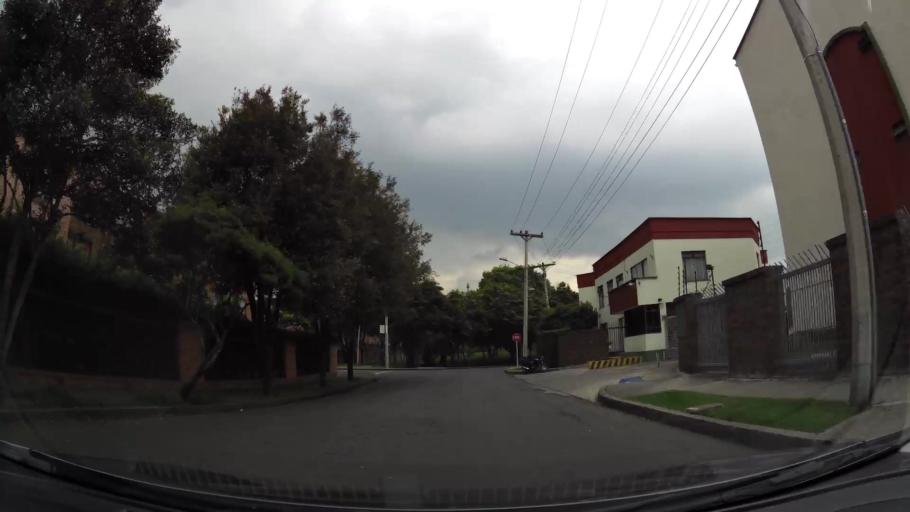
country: CO
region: Cundinamarca
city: La Calera
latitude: 4.7359
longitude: -74.0332
